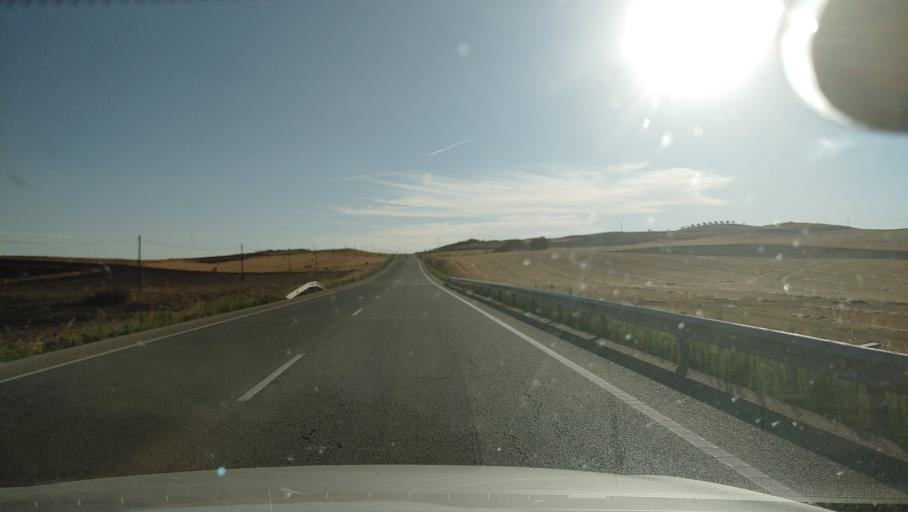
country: ES
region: Castille-La Mancha
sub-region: Provincia de Ciudad Real
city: Fuenllana
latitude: 38.7501
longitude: -2.9675
